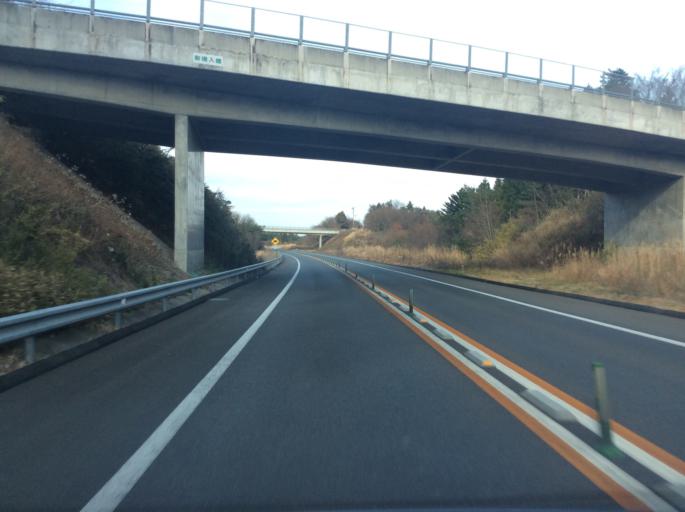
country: JP
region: Fukushima
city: Iwaki
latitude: 37.2523
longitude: 140.9908
